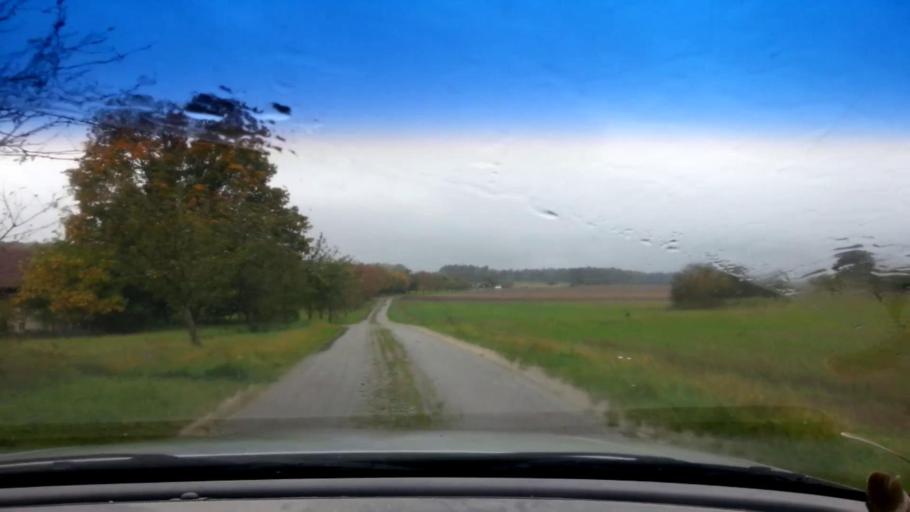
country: DE
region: Bavaria
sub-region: Upper Franconia
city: Altendorf
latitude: 50.0457
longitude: 11.1769
